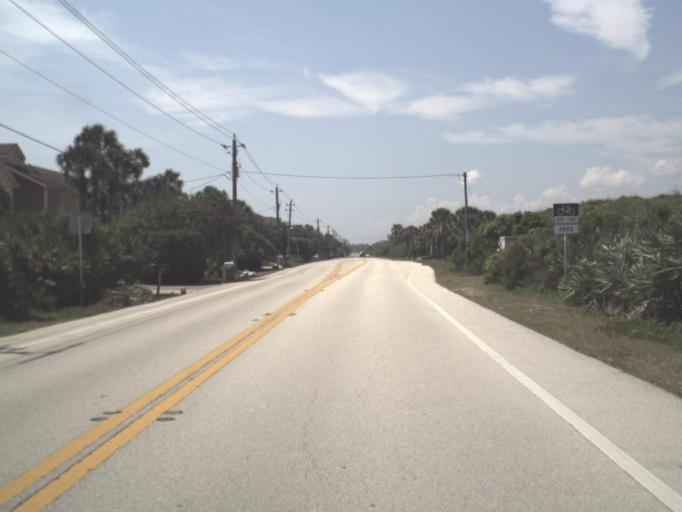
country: US
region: Florida
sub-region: Saint Johns County
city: Villano Beach
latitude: 29.9847
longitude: -81.3138
